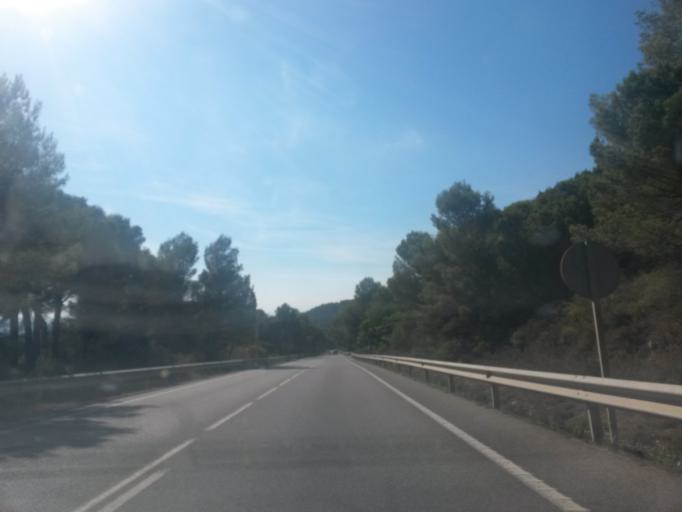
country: ES
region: Catalonia
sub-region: Provincia de Girona
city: Regencos
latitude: 41.9517
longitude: 3.1864
